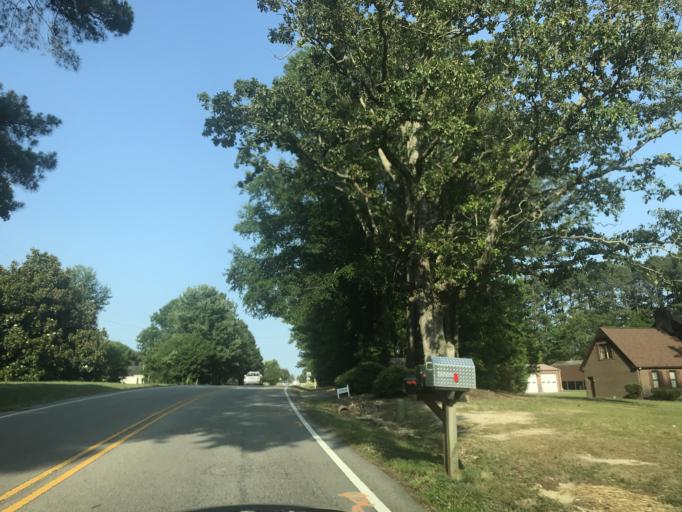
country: US
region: North Carolina
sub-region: Wake County
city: Knightdale
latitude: 35.8283
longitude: -78.5102
